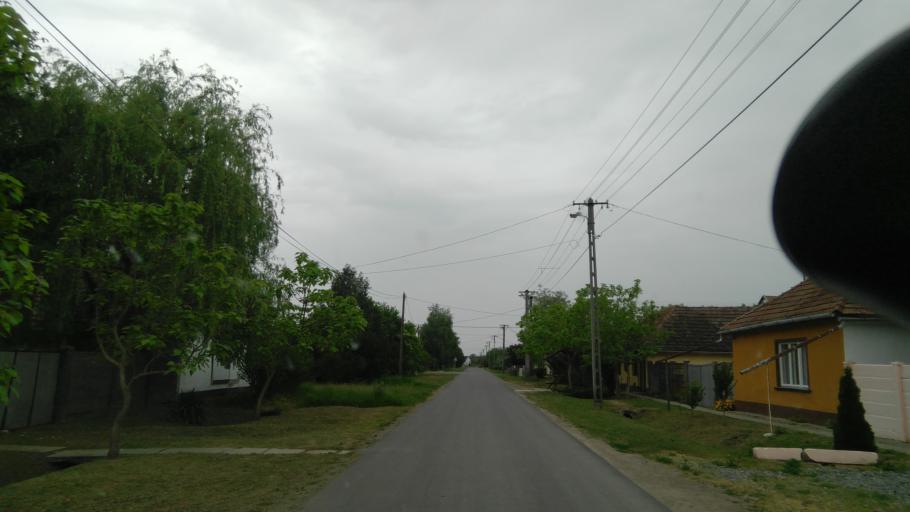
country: HU
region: Bekes
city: Doboz
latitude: 46.7289
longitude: 21.2473
